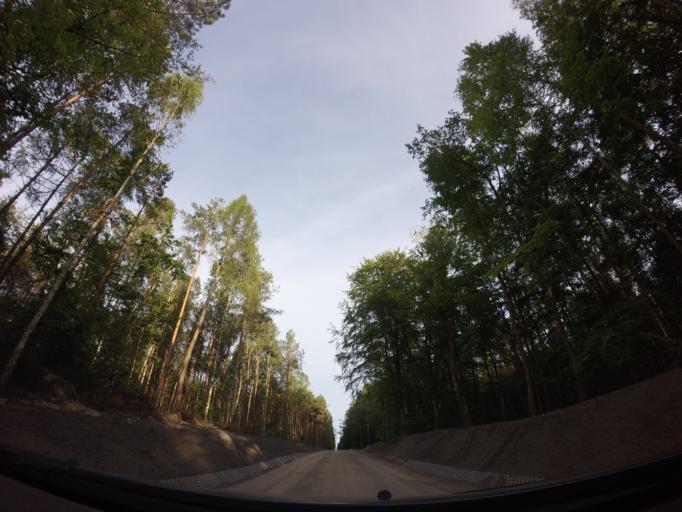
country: PL
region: West Pomeranian Voivodeship
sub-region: Powiat choszczenski
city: Bierzwnik
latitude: 53.0229
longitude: 15.6048
